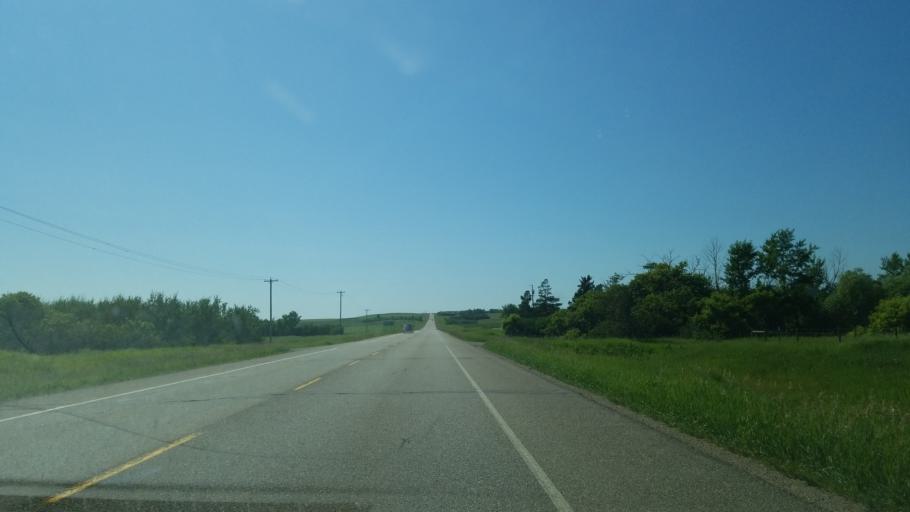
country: CA
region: Alberta
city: Provost
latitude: 52.3613
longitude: -110.1241
